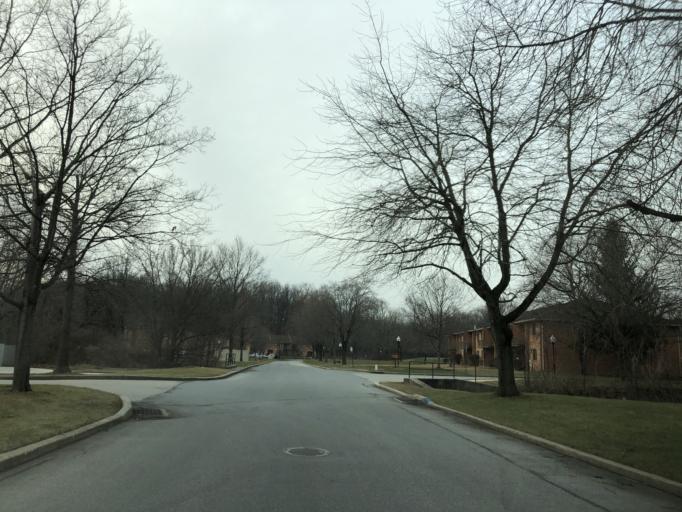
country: US
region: Pennsylvania
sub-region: Chester County
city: Exton
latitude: 40.0362
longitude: -75.6341
